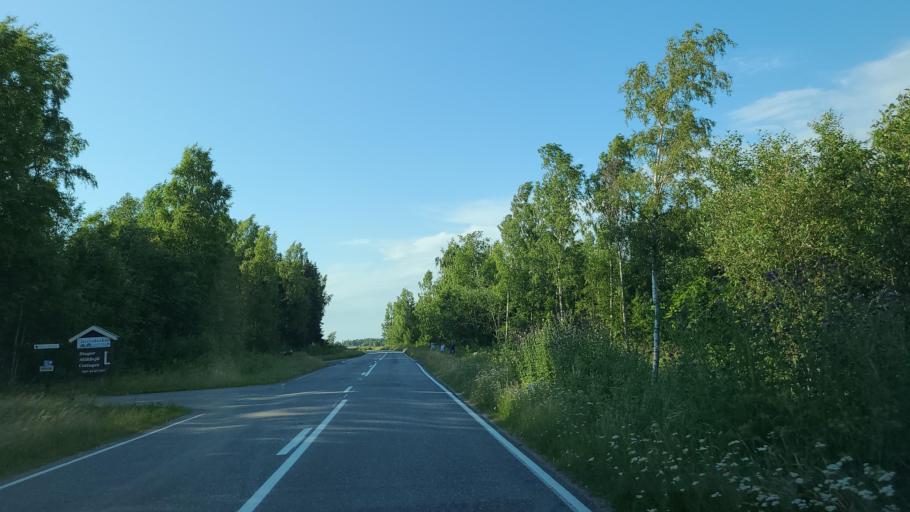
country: FI
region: Ostrobothnia
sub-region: Vaasa
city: Replot
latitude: 63.2785
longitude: 21.3415
